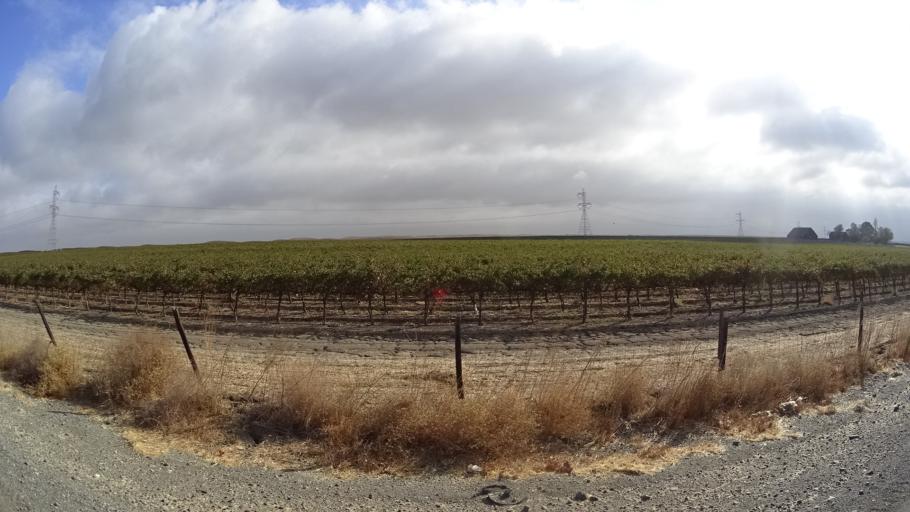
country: US
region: California
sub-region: Yolo County
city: Esparto
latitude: 38.7843
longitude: -122.0074
